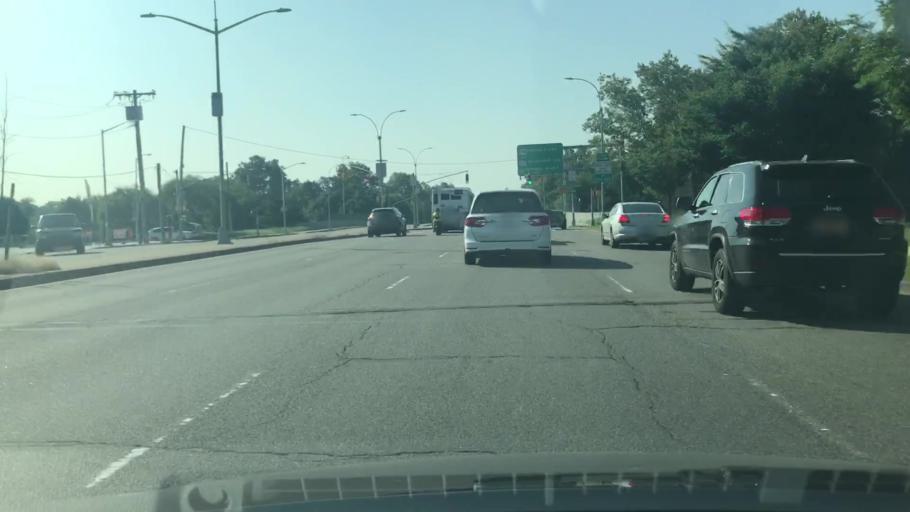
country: US
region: New York
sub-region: Queens County
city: Borough of Queens
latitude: 40.6700
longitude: -73.8428
